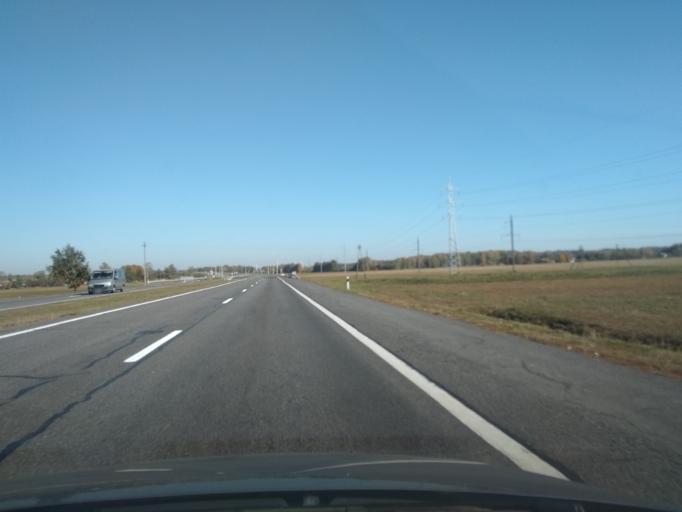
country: BY
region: Brest
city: Horad Kobryn
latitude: 52.1983
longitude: 24.4144
